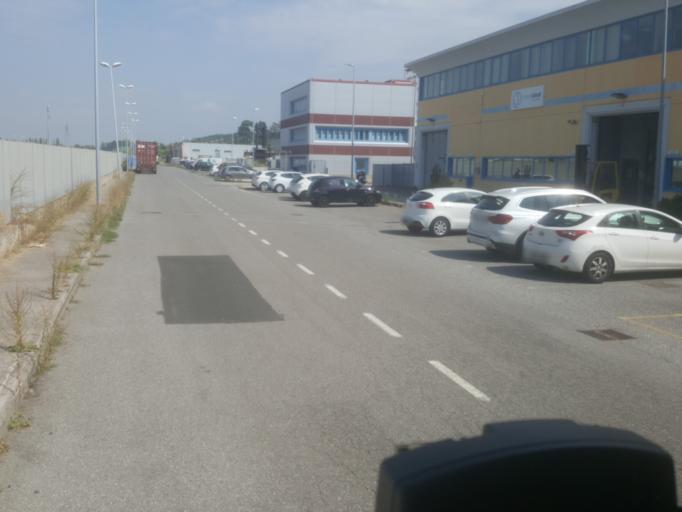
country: IT
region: Tuscany
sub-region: Provincia di Livorno
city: Guasticce
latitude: 43.5949
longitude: 10.3948
